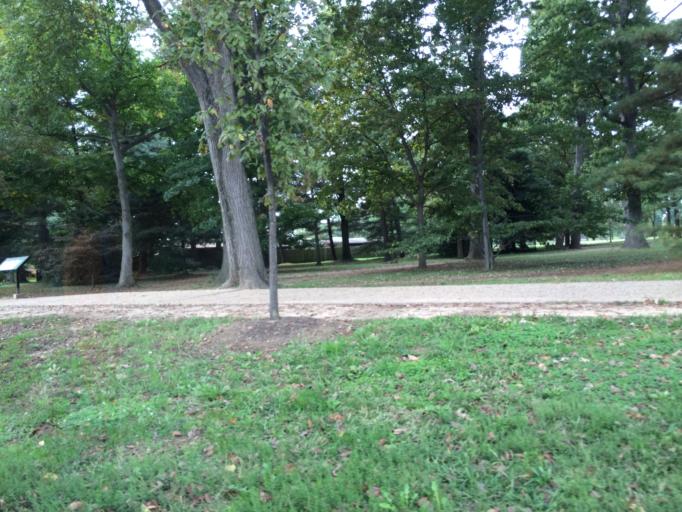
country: US
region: Washington, D.C.
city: Washington, D.C.
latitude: 38.8871
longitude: -77.0445
